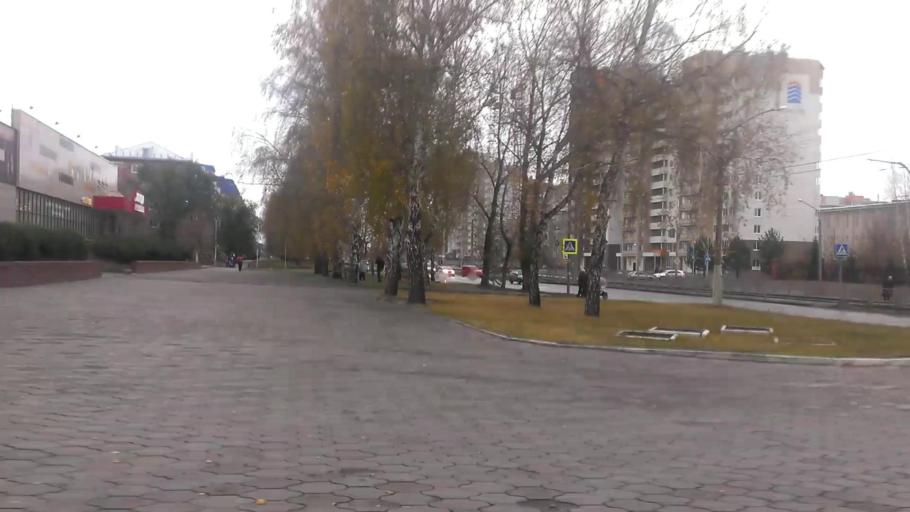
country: RU
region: Altai Krai
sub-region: Gorod Barnaulskiy
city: Barnaul
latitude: 53.3609
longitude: 83.6900
